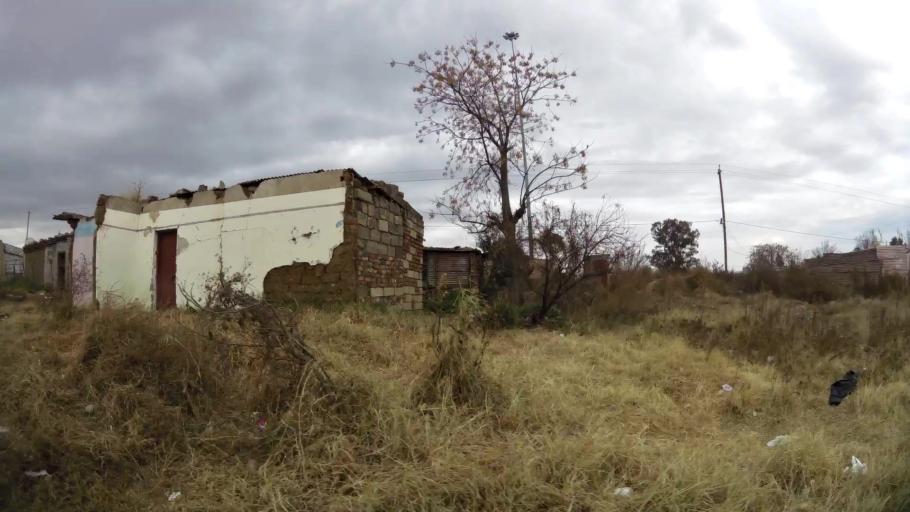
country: ZA
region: Orange Free State
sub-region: Fezile Dabi District Municipality
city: Kroonstad
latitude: -27.6473
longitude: 27.2161
